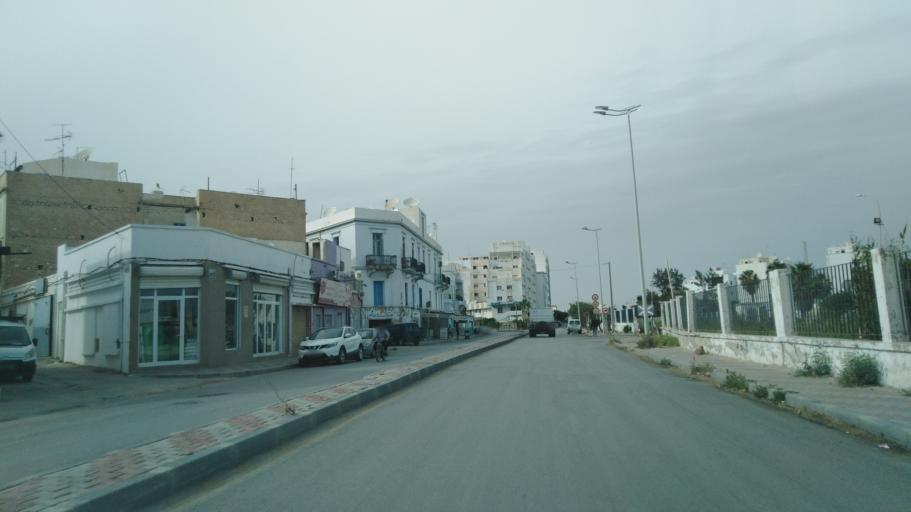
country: TN
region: Safaqis
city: Sfax
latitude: 34.7410
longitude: 10.7638
